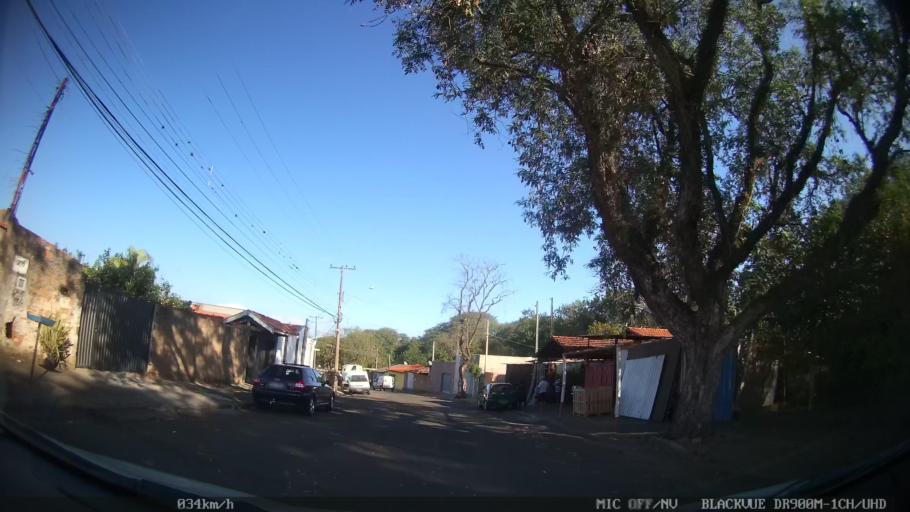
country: BR
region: Sao Paulo
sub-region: Piracicaba
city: Piracicaba
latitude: -22.6862
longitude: -47.6354
